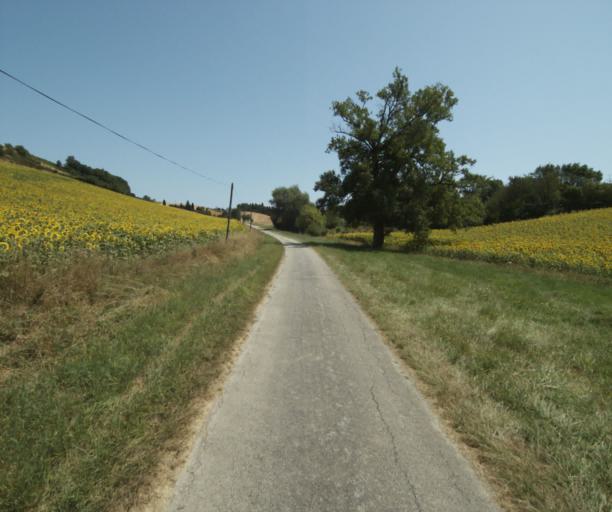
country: FR
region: Midi-Pyrenees
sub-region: Departement de la Haute-Garonne
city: Saint-Felix-Lauragais
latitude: 43.4468
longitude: 1.8672
